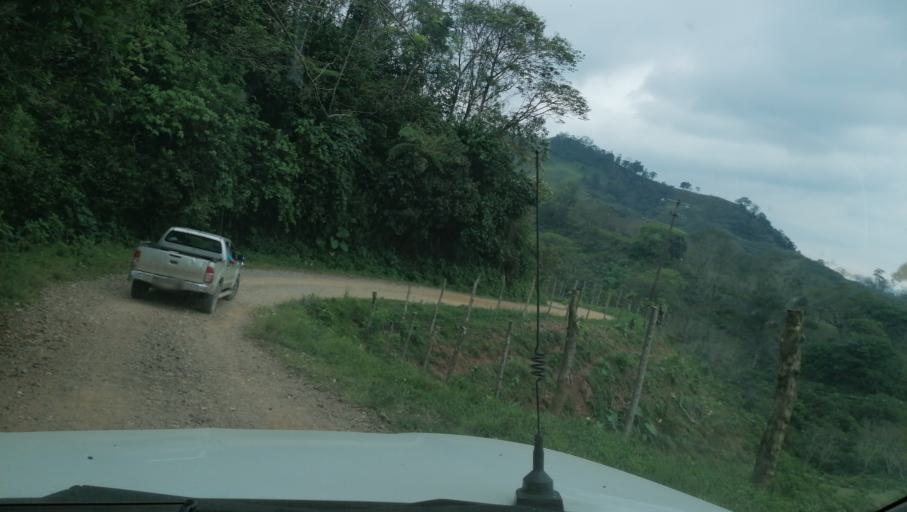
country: MX
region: Chiapas
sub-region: Francisco Leon
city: San Miguel la Sardina
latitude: 17.3319
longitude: -93.3107
